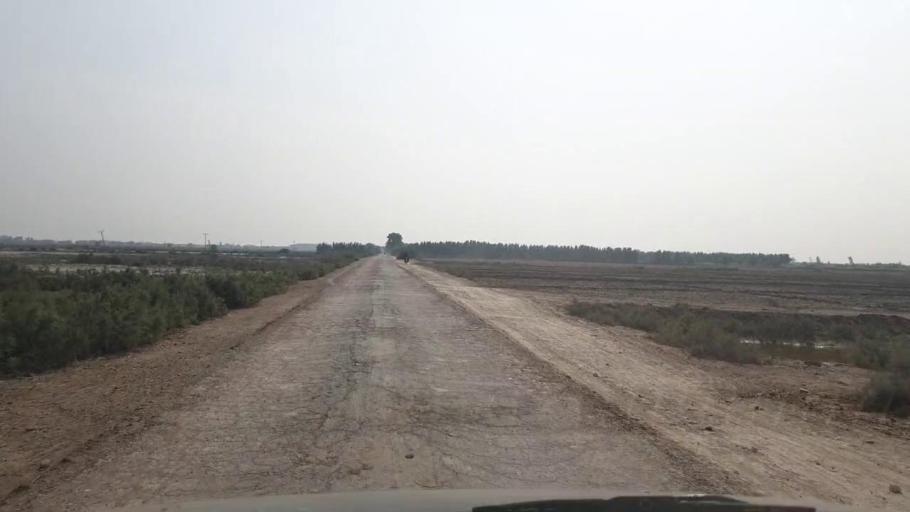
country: PK
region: Sindh
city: Tando Muhammad Khan
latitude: 25.0456
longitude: 68.3900
